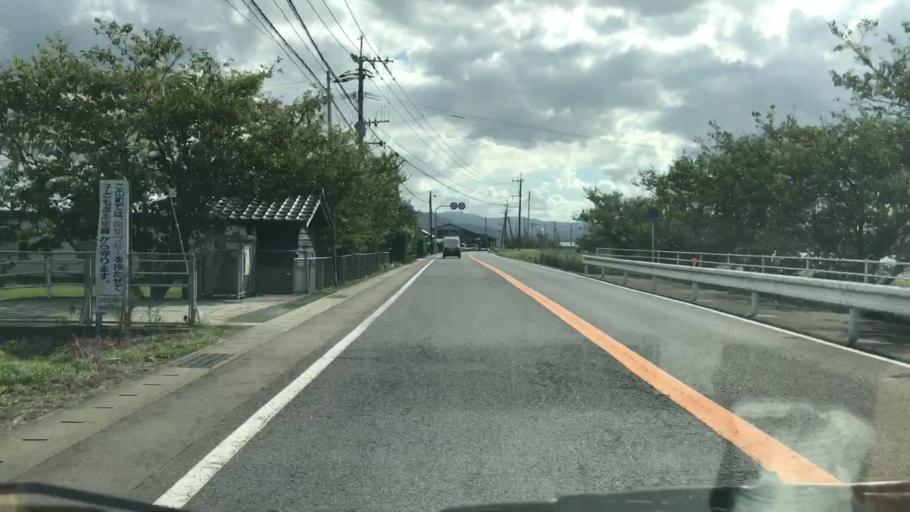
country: JP
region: Saga Prefecture
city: Kashima
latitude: 33.1596
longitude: 130.1636
